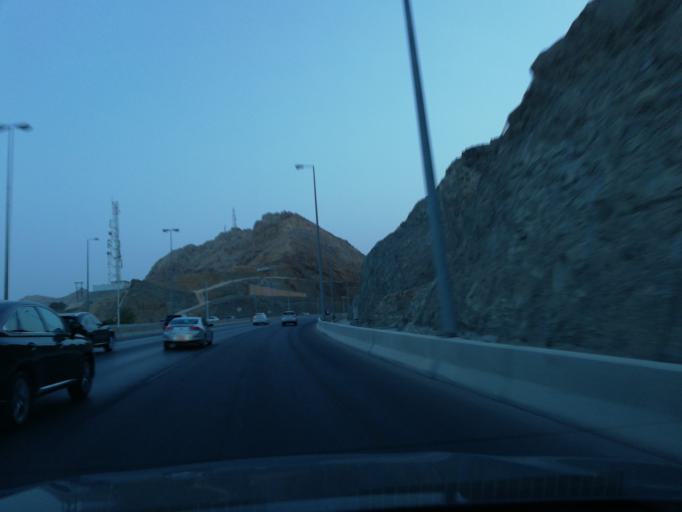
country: OM
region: Muhafazat Masqat
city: Muscat
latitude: 23.6168
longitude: 58.5331
